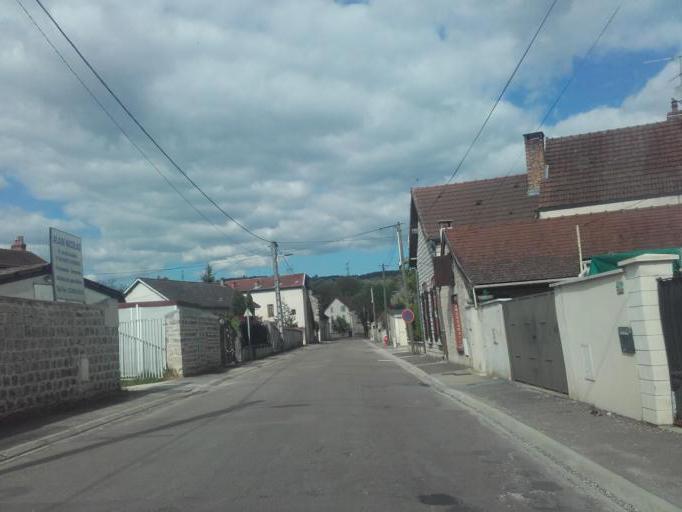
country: FR
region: Bourgogne
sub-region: Departement de la Cote-d'Or
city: Nuits-Saint-Georges
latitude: 47.1324
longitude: 4.9541
